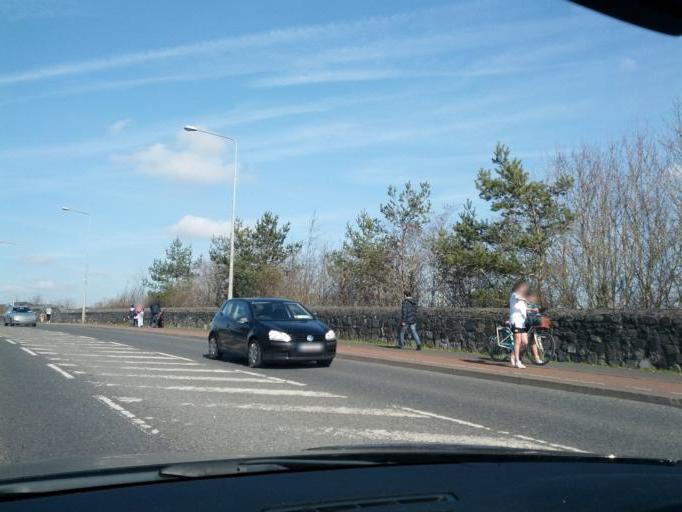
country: IE
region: Leinster
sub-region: Kildare
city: Maynooth
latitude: 53.3778
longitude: -6.5876
